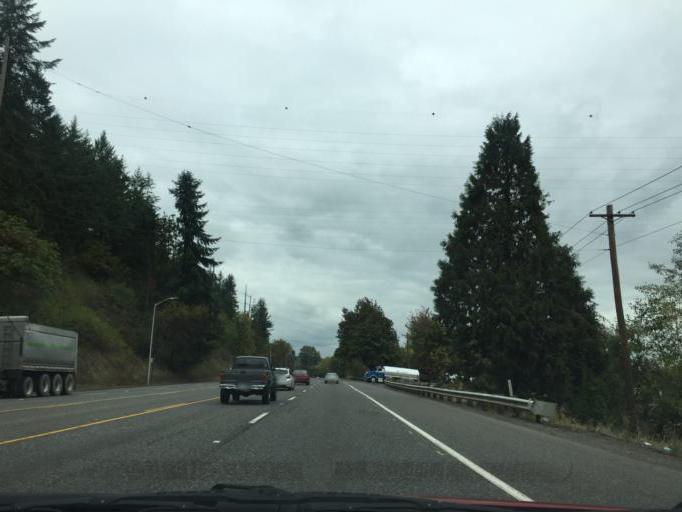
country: US
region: Oregon
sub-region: Washington County
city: Oak Hills
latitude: 45.6096
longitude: -122.7950
